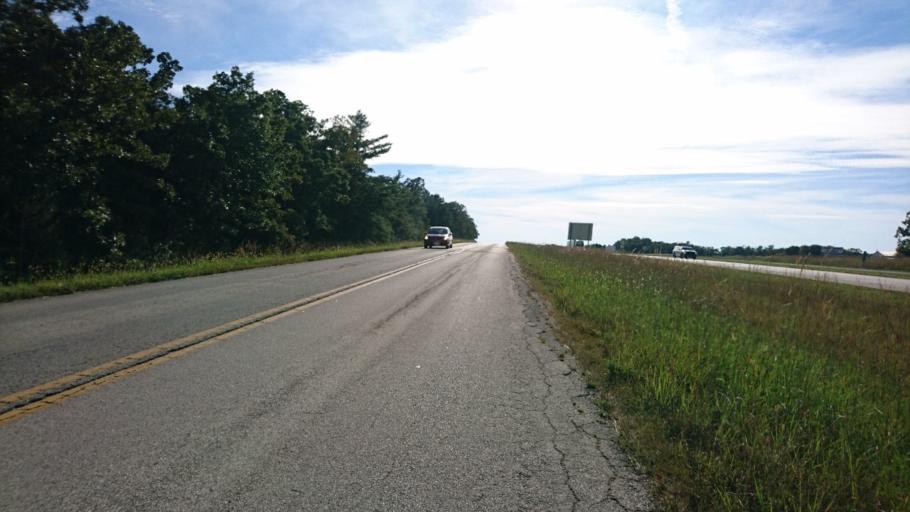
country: US
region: Missouri
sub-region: Crawford County
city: Bourbon
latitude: 38.1153
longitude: -91.3241
